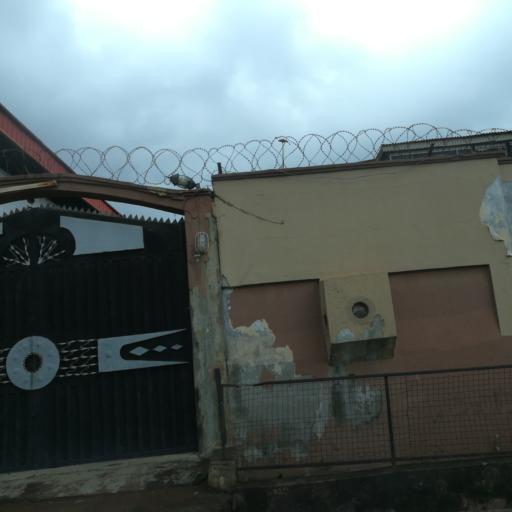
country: NG
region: Lagos
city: Agege
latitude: 6.6068
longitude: 3.3058
